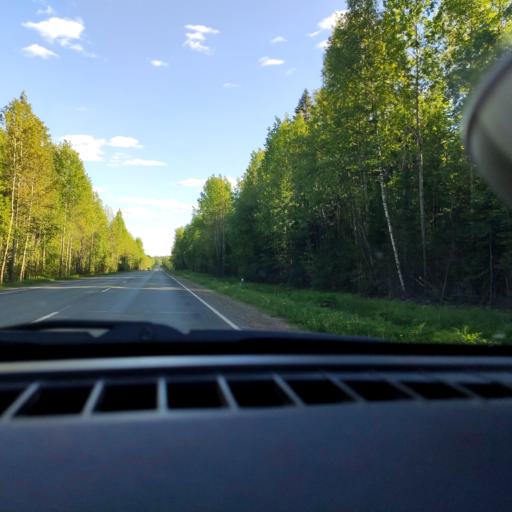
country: RU
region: Perm
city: Polazna
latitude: 58.2831
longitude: 56.1645
